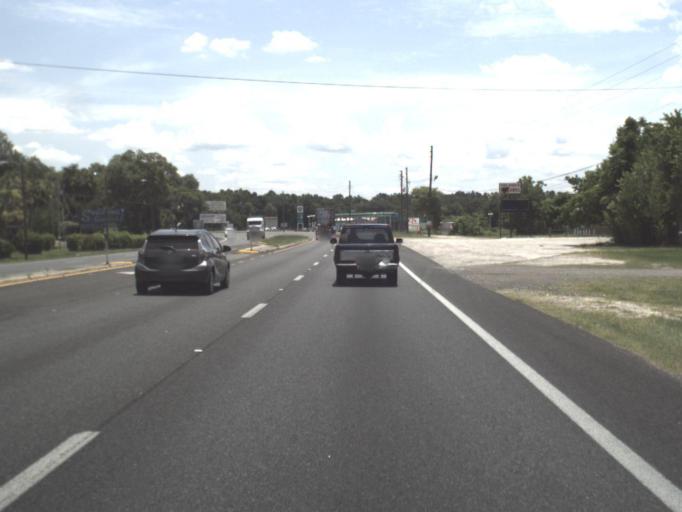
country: US
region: Florida
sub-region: Levy County
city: Manatee Road
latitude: 29.5863
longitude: -82.9585
